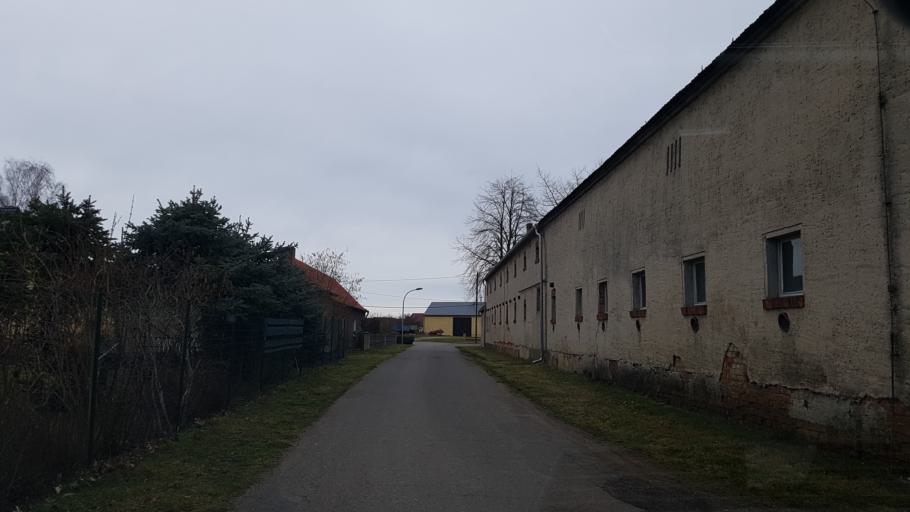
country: DE
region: Brandenburg
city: Bad Liebenwerda
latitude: 51.5103
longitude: 13.3475
